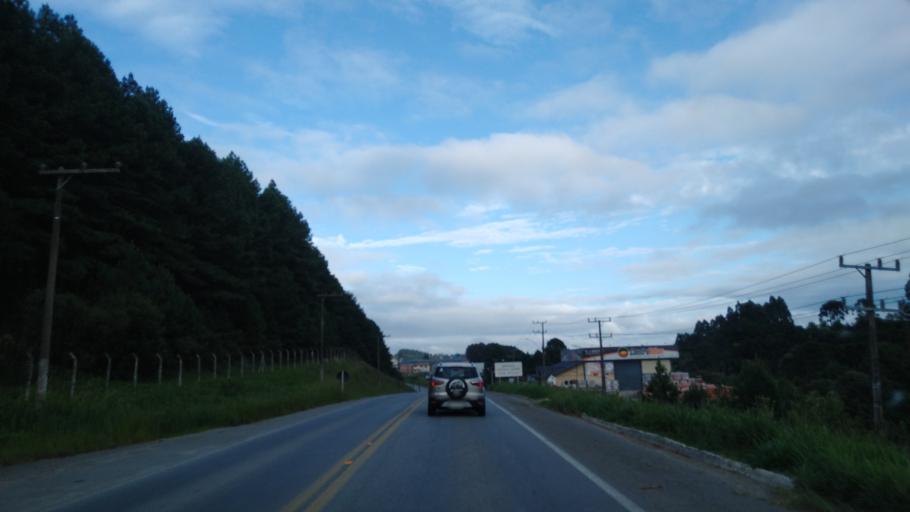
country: BR
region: Santa Catarina
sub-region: Rio Negrinho
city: Rio Negrinho
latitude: -26.2376
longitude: -49.4845
